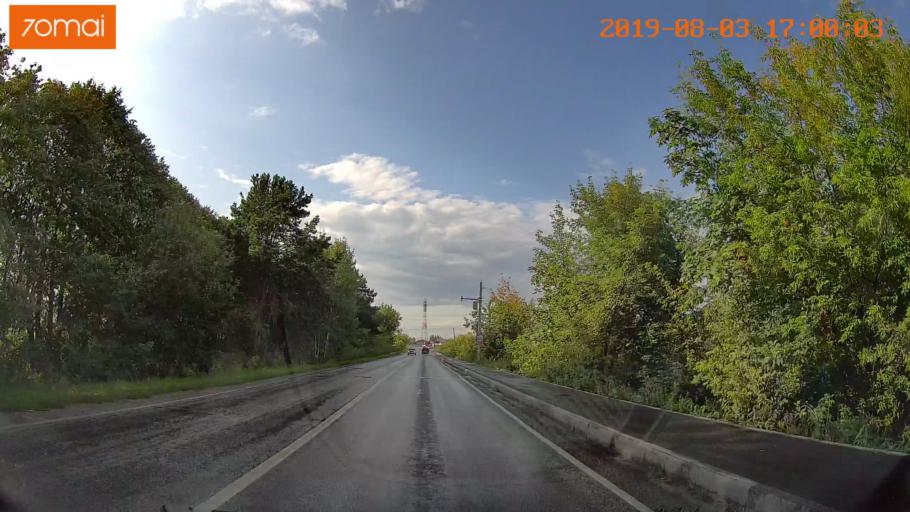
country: RU
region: Moskovskaya
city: Voskresensk
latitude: 55.3342
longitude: 38.6202
